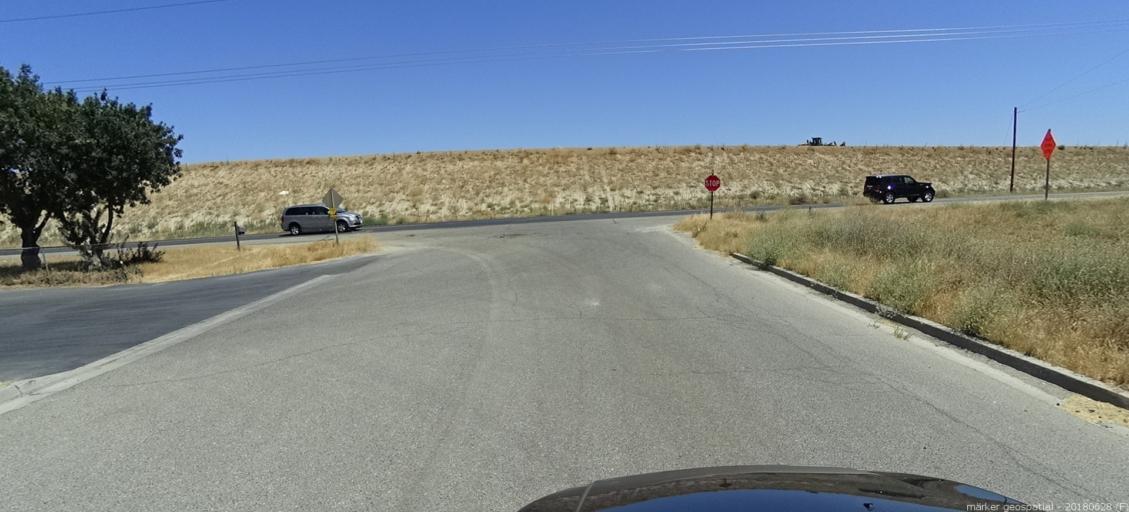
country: US
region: California
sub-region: Madera County
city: Parksdale
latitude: 36.9230
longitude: -119.9790
